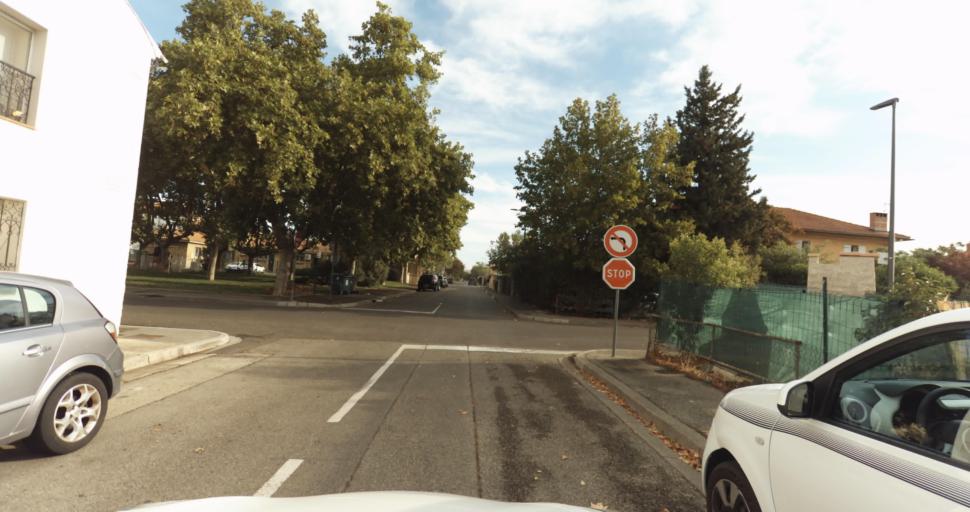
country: FR
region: Provence-Alpes-Cote d'Azur
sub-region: Departement des Bouches-du-Rhone
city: Miramas
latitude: 43.5831
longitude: 4.9974
